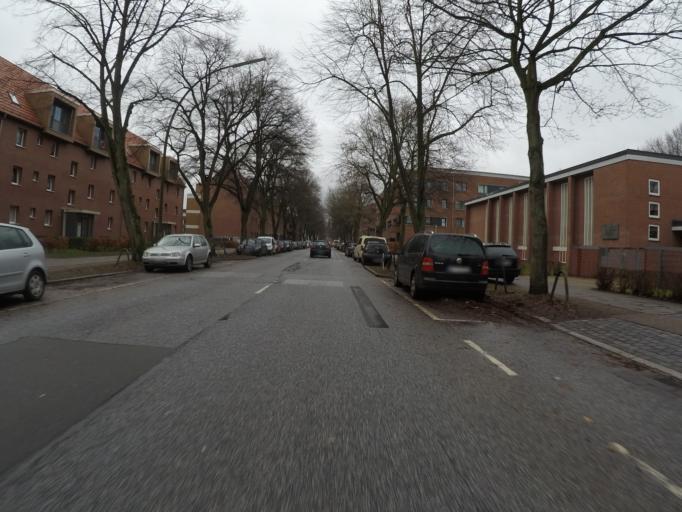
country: DE
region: Hamburg
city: Kleiner Grasbrook
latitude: 53.5087
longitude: 9.9865
